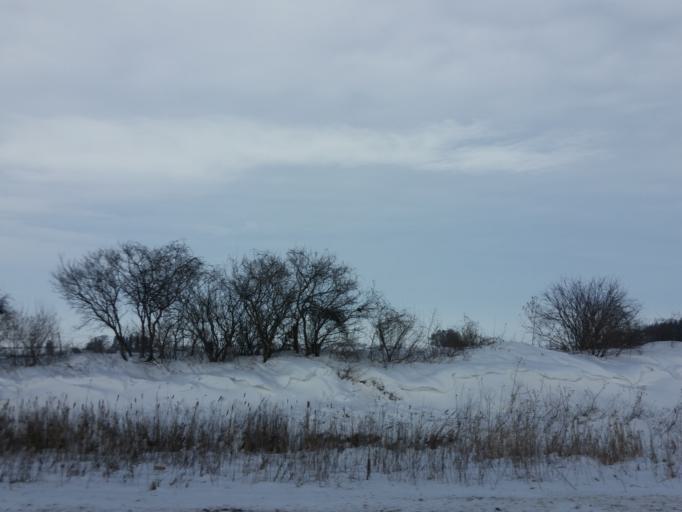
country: US
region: Iowa
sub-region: Delaware County
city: Manchester
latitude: 42.4646
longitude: -91.6255
